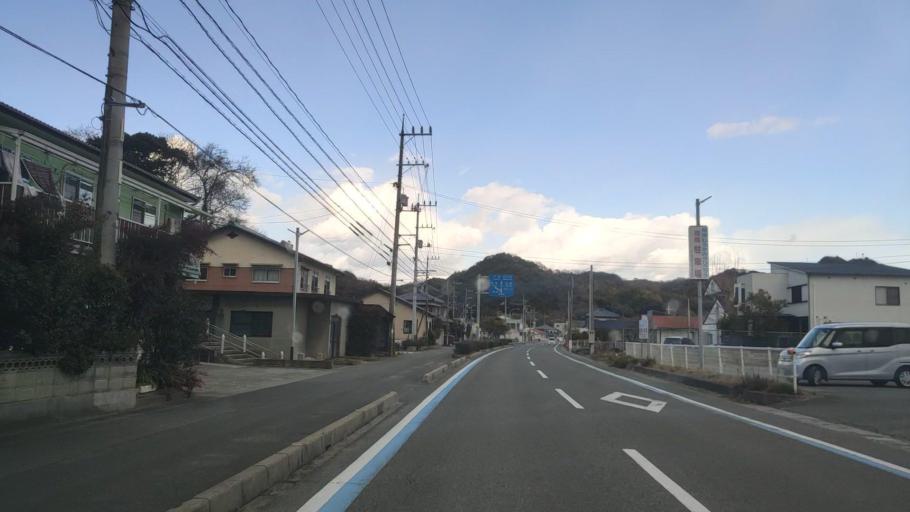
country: JP
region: Hiroshima
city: Innoshima
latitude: 34.2026
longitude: 133.0921
